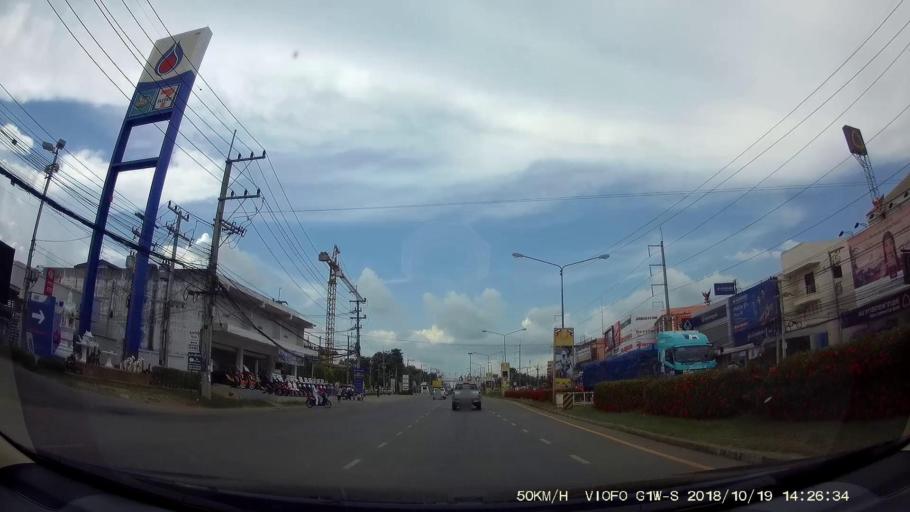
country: TH
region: Chaiyaphum
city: Kaeng Khro
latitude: 16.1072
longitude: 102.2595
